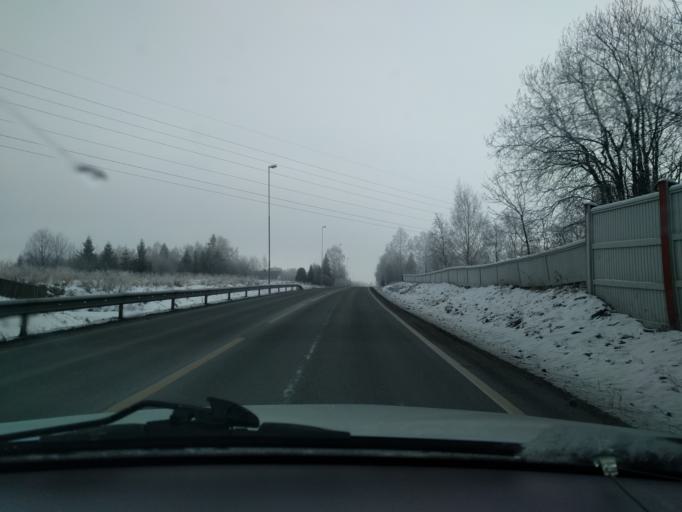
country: NO
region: Hedmark
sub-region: Hamar
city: Hamar
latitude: 60.8027
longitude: 11.1385
